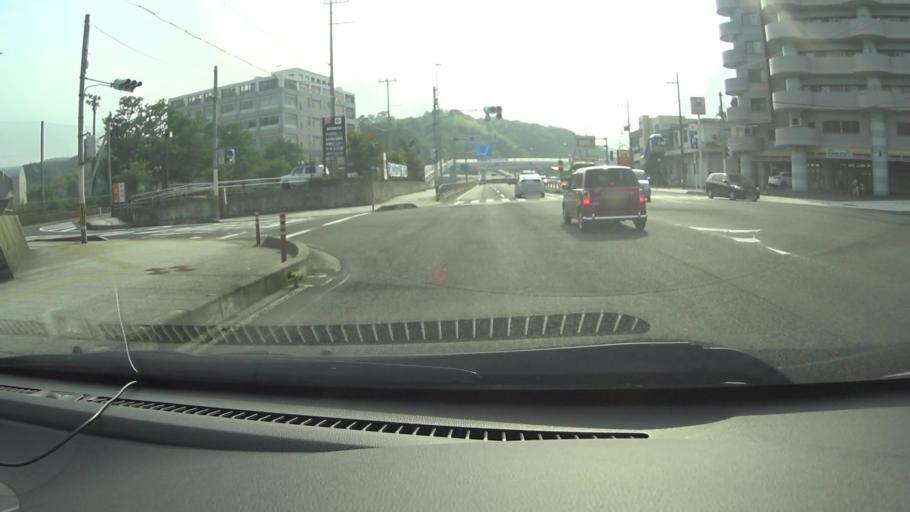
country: JP
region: Kyoto
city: Maizuru
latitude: 35.4766
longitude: 135.3695
